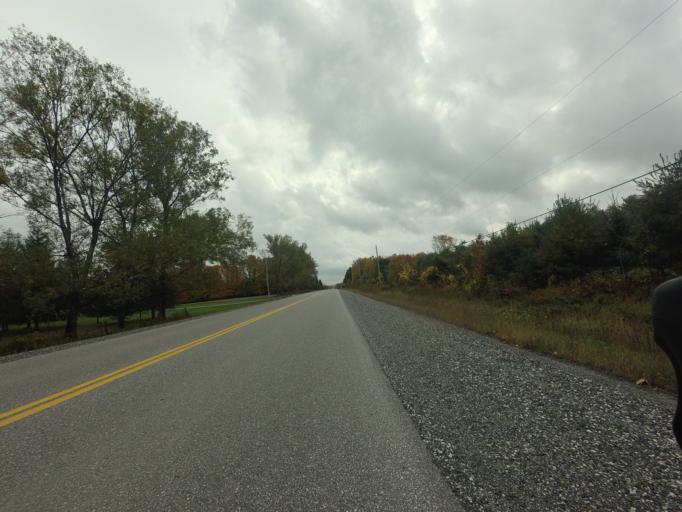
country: CA
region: Ontario
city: Perth
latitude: 45.0976
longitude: -76.4653
